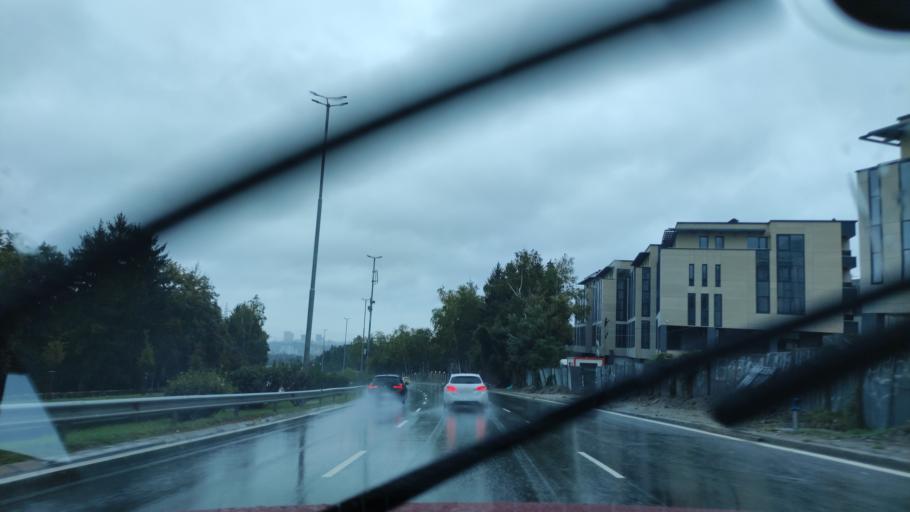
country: BG
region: Sofia-Capital
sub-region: Stolichna Obshtina
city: Sofia
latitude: 42.6491
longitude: 23.2755
